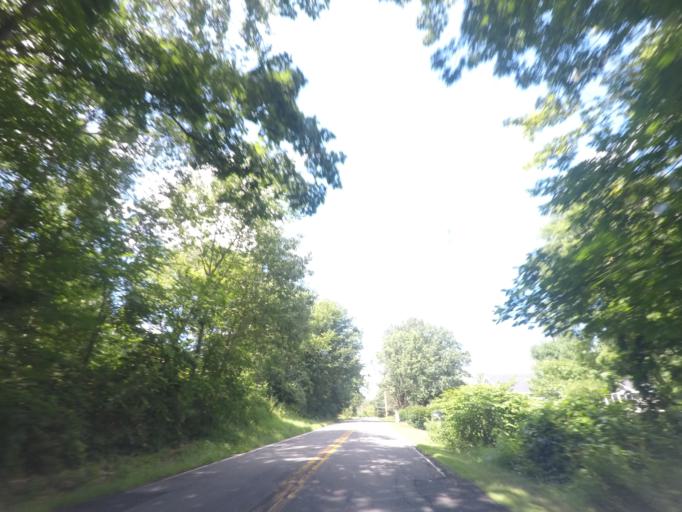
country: US
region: New York
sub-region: Albany County
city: Voorheesville
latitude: 42.7169
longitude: -73.9595
